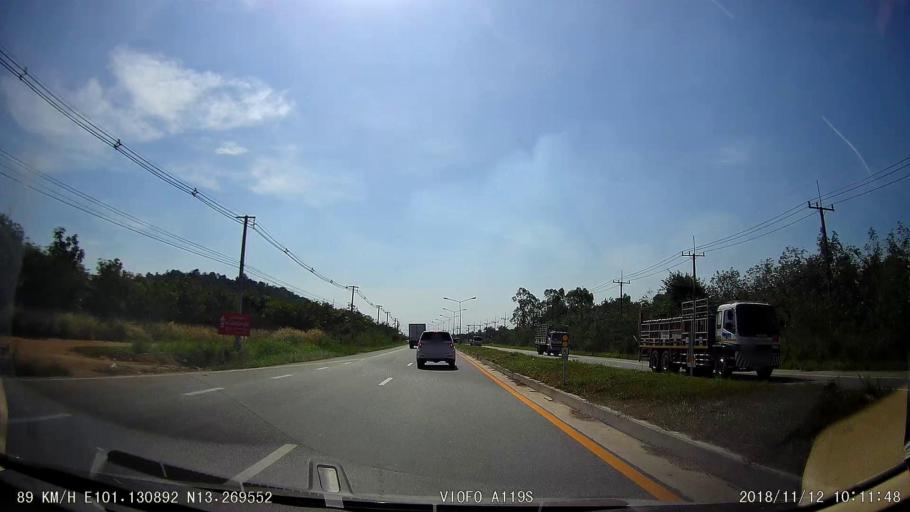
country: TH
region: Chon Buri
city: Ban Bueng
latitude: 13.2692
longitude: 101.1311
